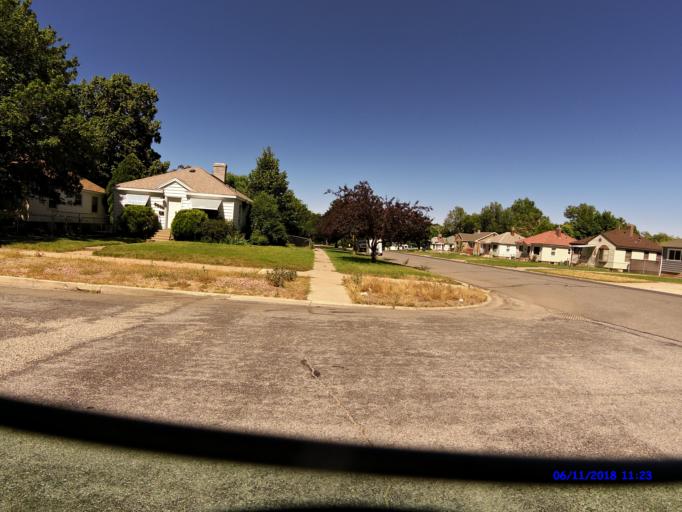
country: US
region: Utah
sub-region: Weber County
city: Ogden
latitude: 41.2244
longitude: -111.9438
